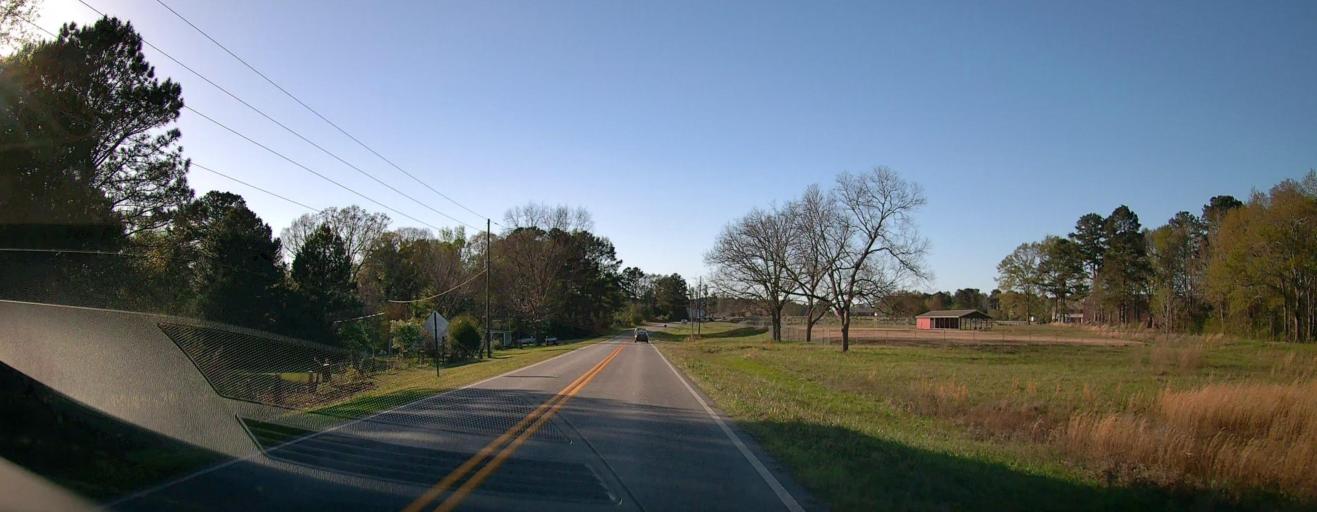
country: US
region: Georgia
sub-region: Butts County
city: Jackson
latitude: 33.3275
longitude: -83.9048
